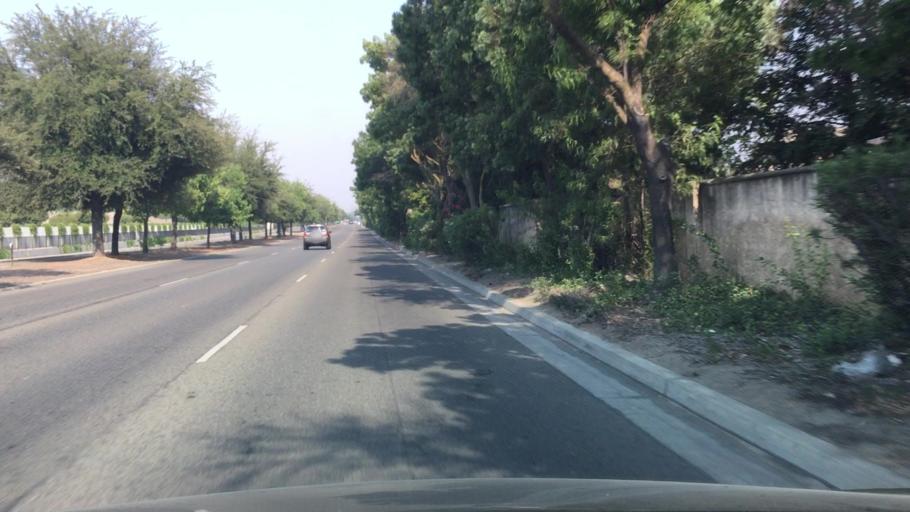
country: US
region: California
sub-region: Fresno County
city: Fresno
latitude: 36.8371
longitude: -119.8434
